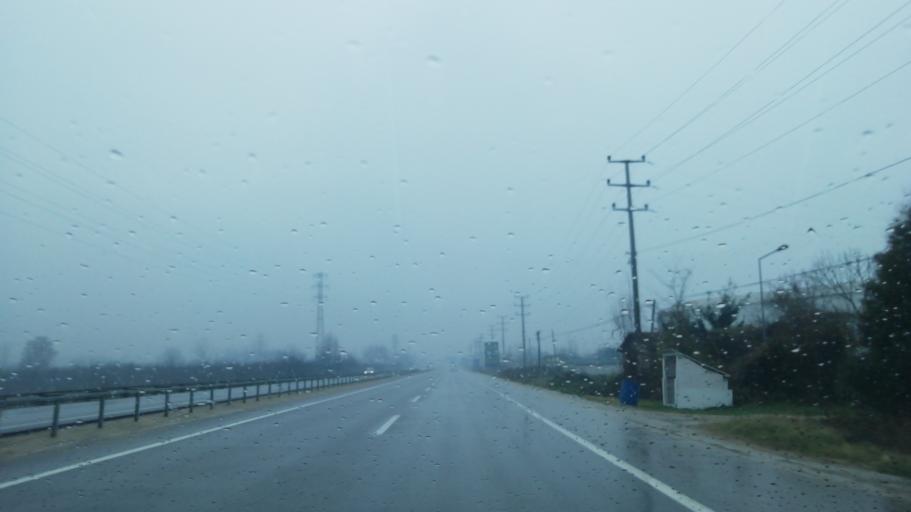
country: TR
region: Sakarya
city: Akyazi
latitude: 40.6381
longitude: 30.6197
